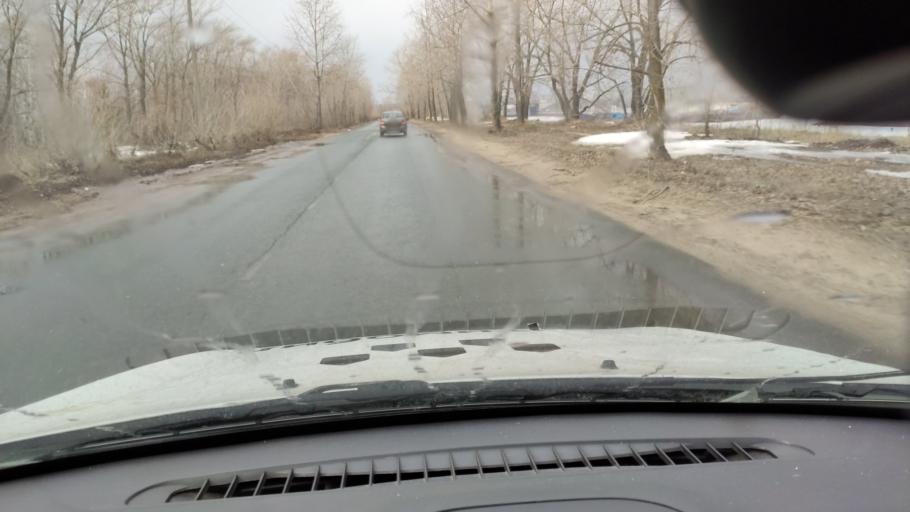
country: RU
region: Samara
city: Zhigulevsk
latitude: 53.4595
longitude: 49.5246
